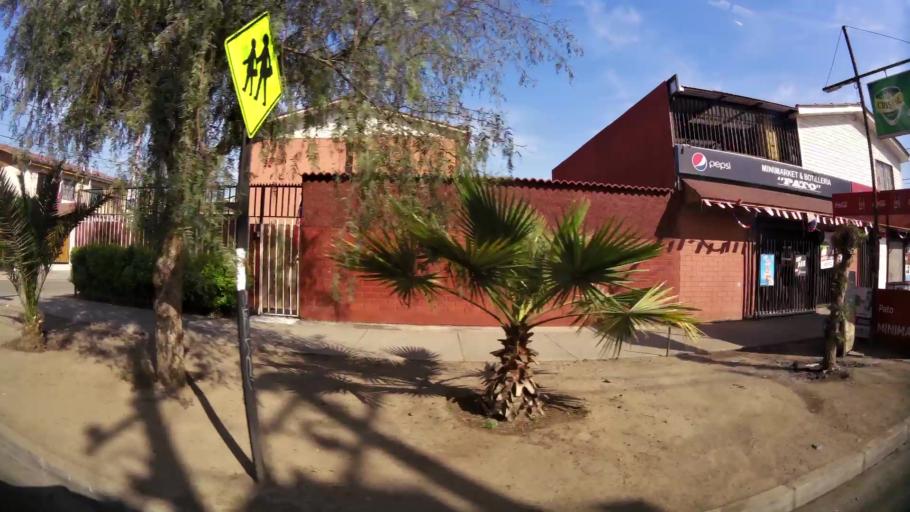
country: CL
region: Santiago Metropolitan
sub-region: Provincia de Santiago
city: Lo Prado
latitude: -33.4629
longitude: -70.7616
